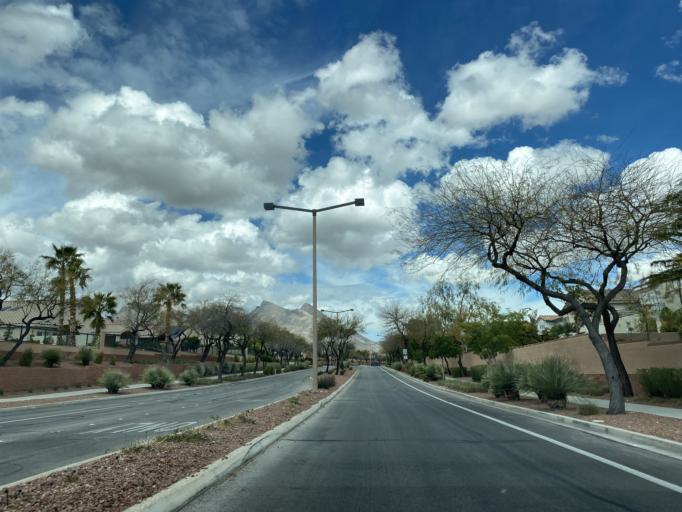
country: US
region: Nevada
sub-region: Clark County
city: Summerlin South
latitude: 36.1828
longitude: -115.3380
